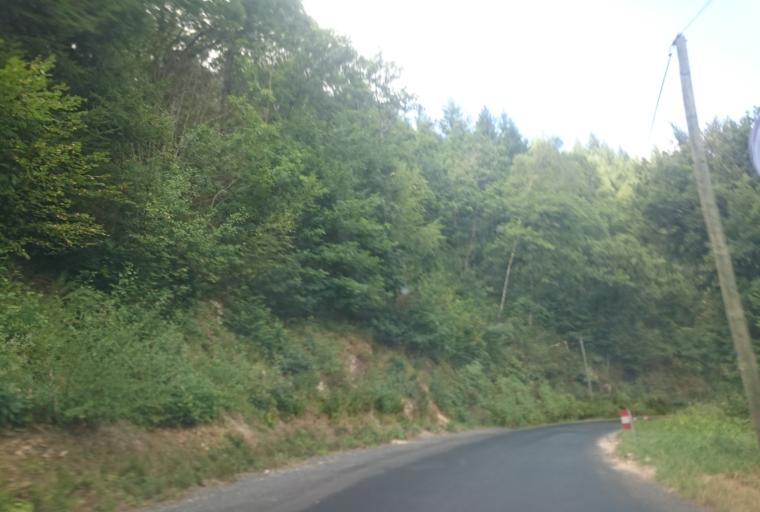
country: FR
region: Auvergne
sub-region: Departement du Cantal
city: Laroquebrou
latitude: 44.9749
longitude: 2.1692
